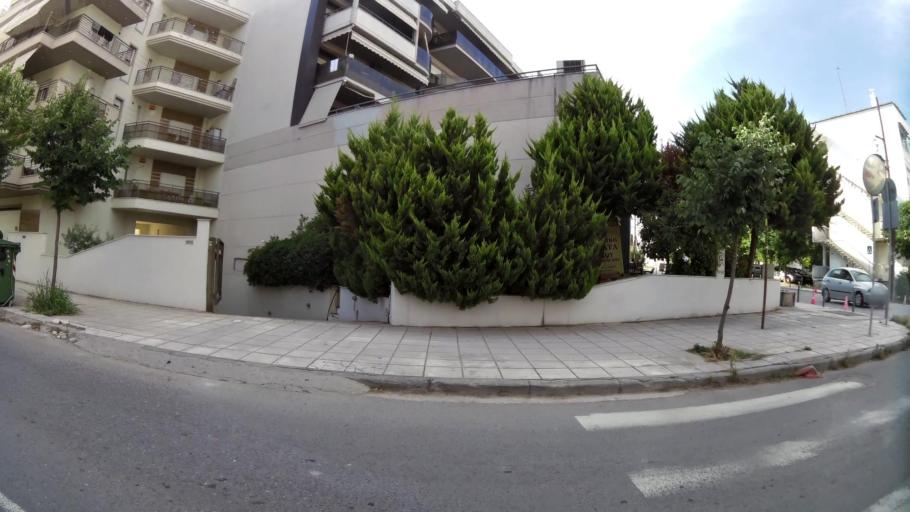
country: GR
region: Central Macedonia
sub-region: Nomos Thessalonikis
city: Kalamaria
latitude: 40.5700
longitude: 22.9705
